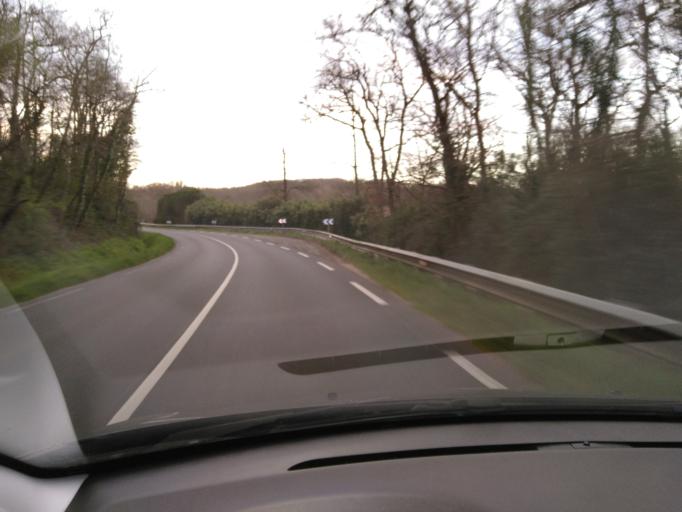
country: FR
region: Midi-Pyrenees
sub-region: Departement de la Haute-Garonne
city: Brax
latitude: 43.6151
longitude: 1.2601
